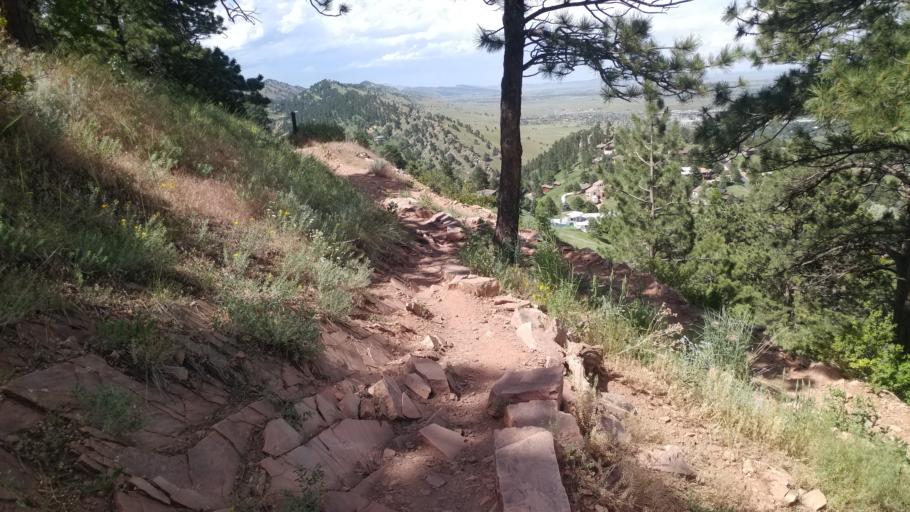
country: US
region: Colorado
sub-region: Boulder County
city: Boulder
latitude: 40.0346
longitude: -105.3010
